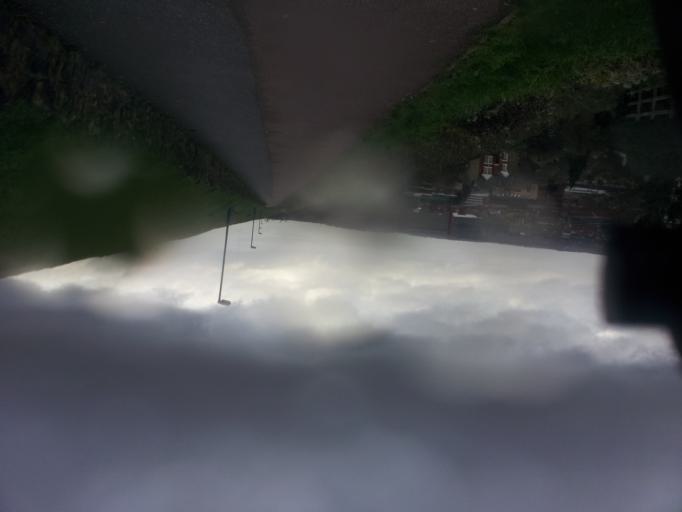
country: GB
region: England
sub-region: Kent
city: Chatham
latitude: 51.3796
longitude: 0.5366
